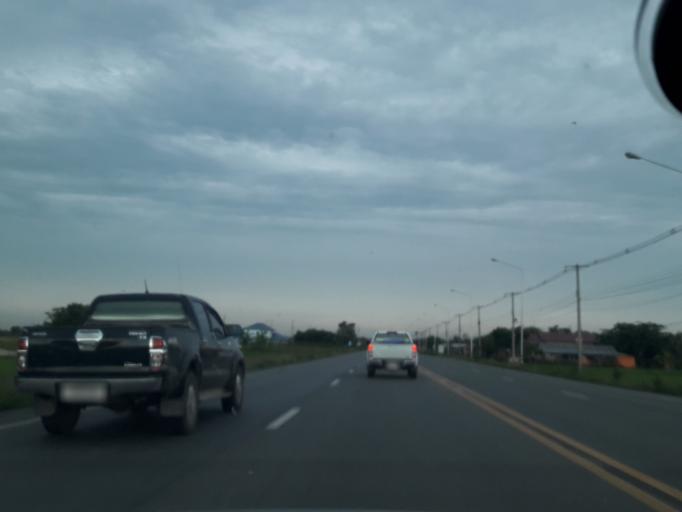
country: TH
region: Pathum Thani
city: Ban Rangsit
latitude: 14.1024
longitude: 100.7472
